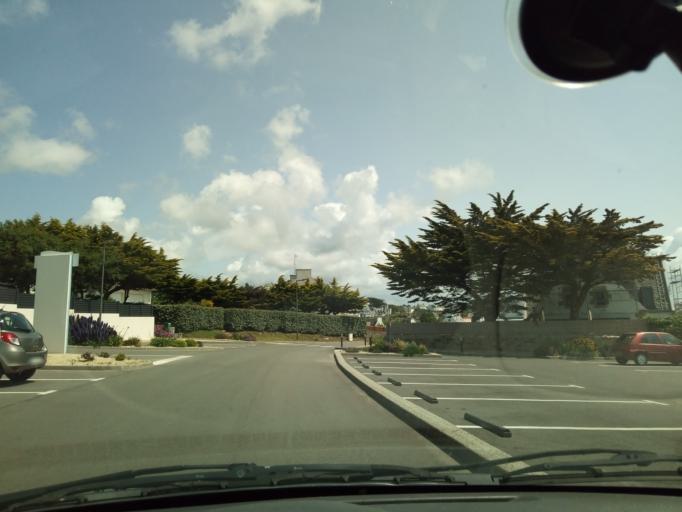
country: FR
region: Brittany
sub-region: Departement du Finistere
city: Audierne
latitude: 48.0115
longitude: -4.5521
